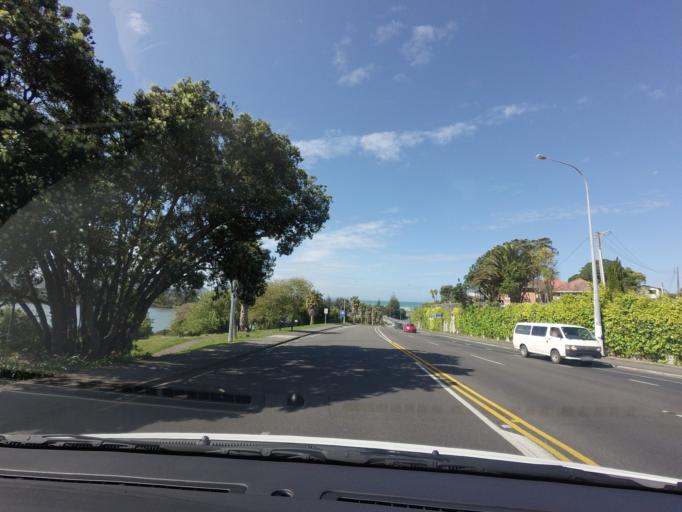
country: NZ
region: Auckland
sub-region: Auckland
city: Rothesay Bay
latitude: -36.6018
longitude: 174.6947
